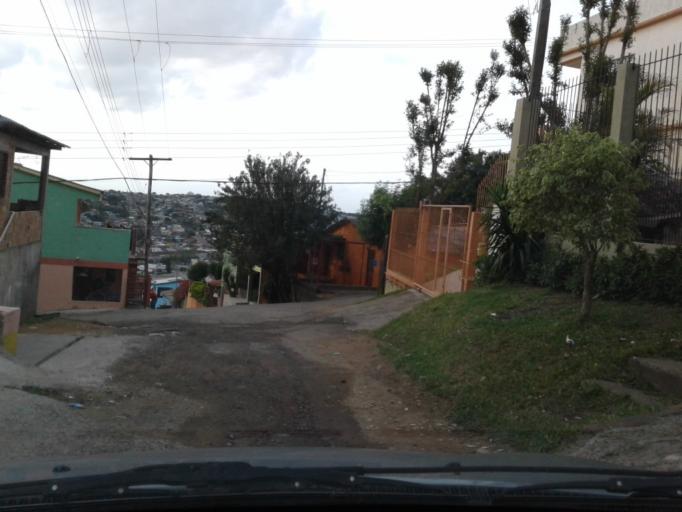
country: BR
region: Rio Grande do Sul
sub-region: Porto Alegre
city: Porto Alegre
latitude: -30.0618
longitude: -51.1441
